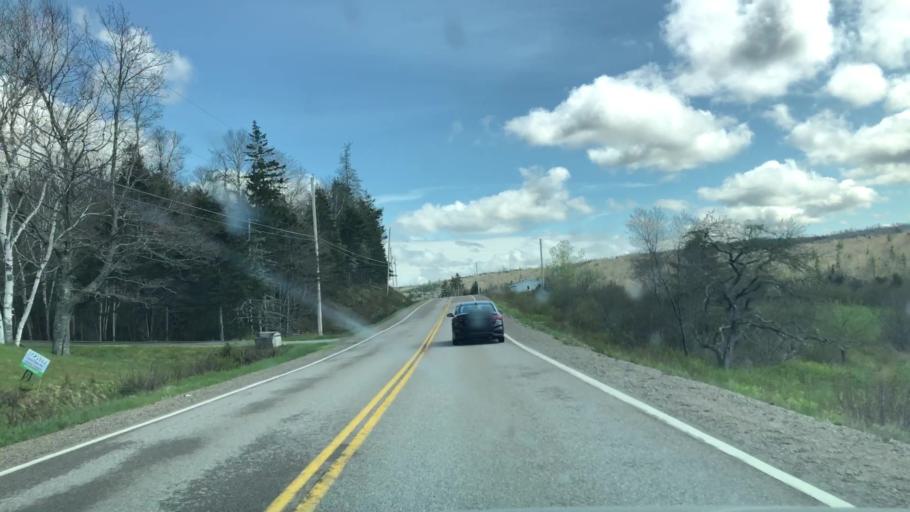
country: CA
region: Nova Scotia
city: Antigonish
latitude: 45.1998
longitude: -62.0028
